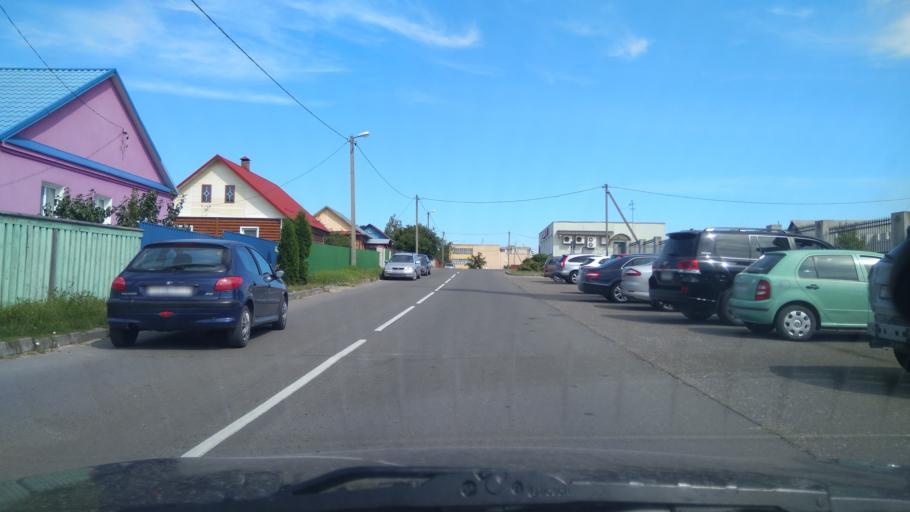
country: BY
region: Brest
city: Ivatsevichy
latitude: 52.7132
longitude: 25.3393
